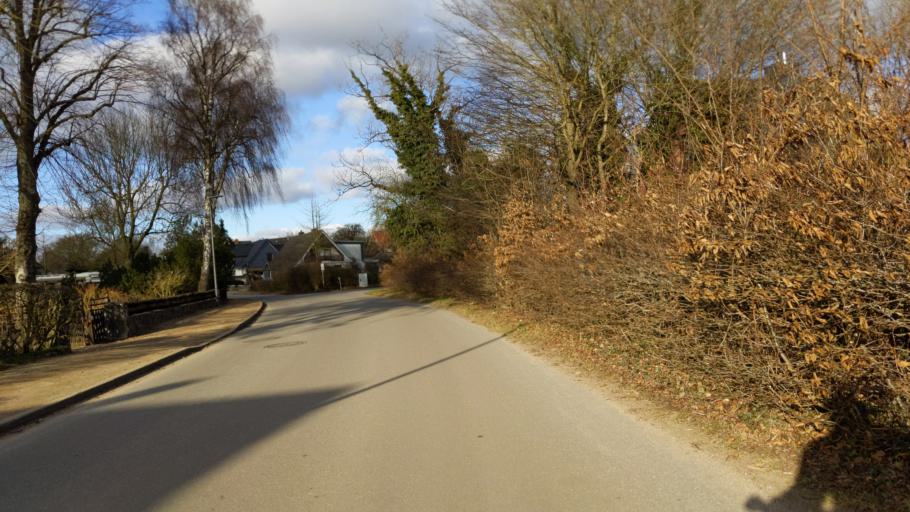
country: DE
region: Schleswig-Holstein
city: Susel
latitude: 54.0827
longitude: 10.7154
